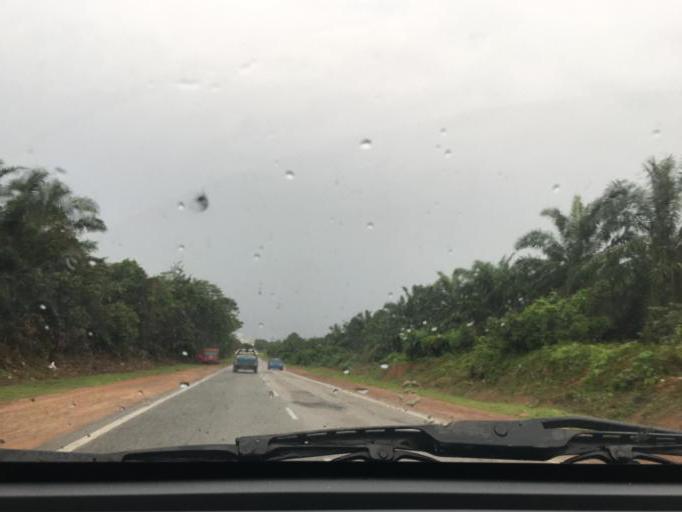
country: MY
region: Kedah
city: Sungai Petani
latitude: 5.6172
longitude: 100.6389
